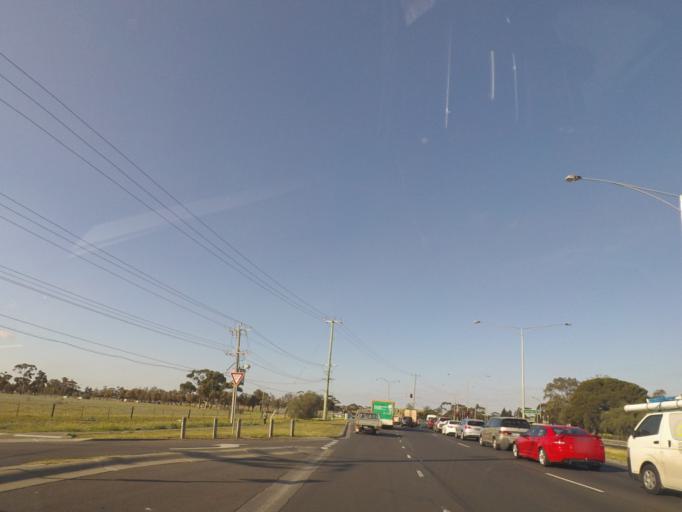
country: AU
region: Victoria
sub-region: Brimbank
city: Deer Park
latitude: -37.7710
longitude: 144.7887
